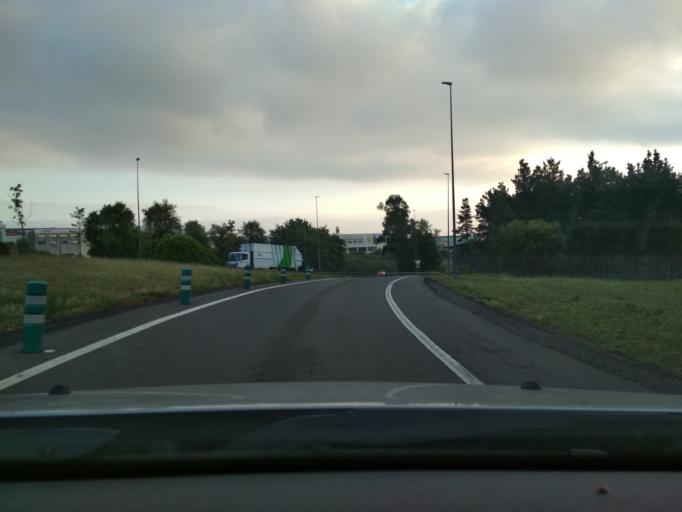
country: ES
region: Galicia
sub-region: Provincia da Coruna
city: Santiago de Compostela
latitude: 42.9075
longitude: -8.5092
